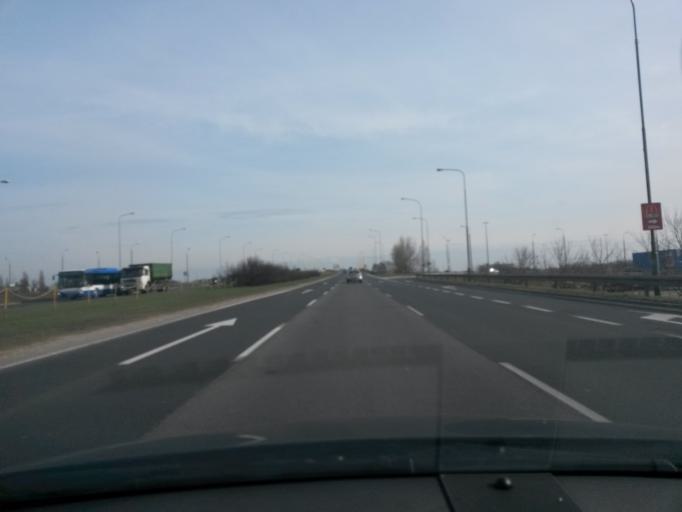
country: PL
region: Greater Poland Voivodeship
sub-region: Poznan
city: Poznan
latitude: 52.3770
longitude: 16.9810
